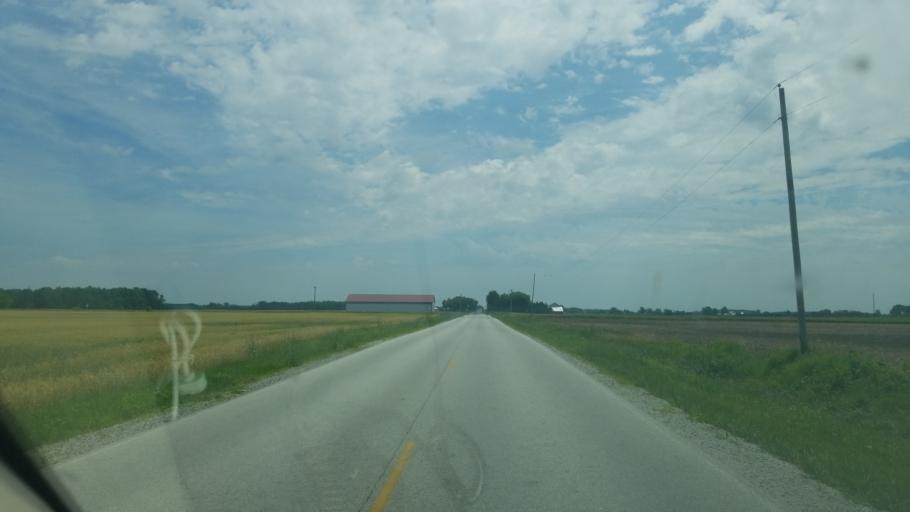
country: US
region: Ohio
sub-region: Wood County
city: Bowling Green
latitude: 41.2967
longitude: -83.6146
